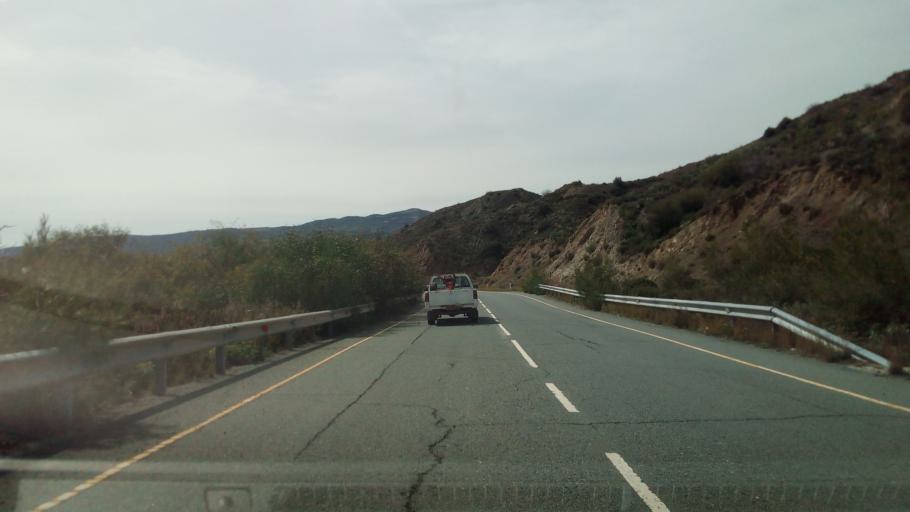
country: CY
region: Limassol
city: Pelendri
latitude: 34.8721
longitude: 32.9311
